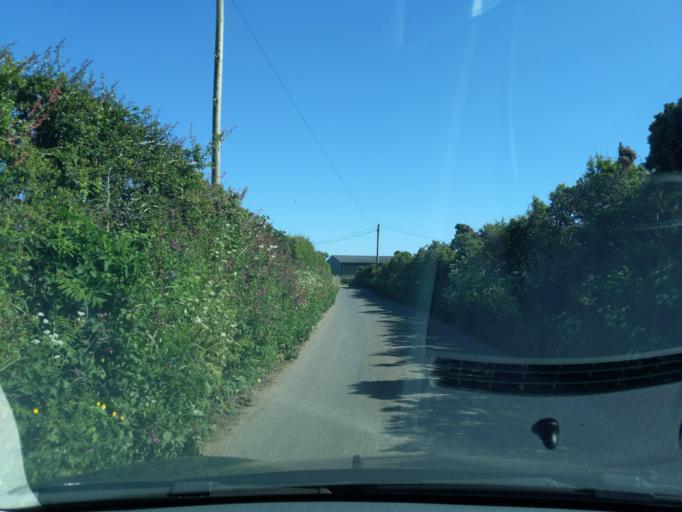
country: GB
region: England
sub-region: Cornwall
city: St. Buryan
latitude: 50.0719
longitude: -5.6132
